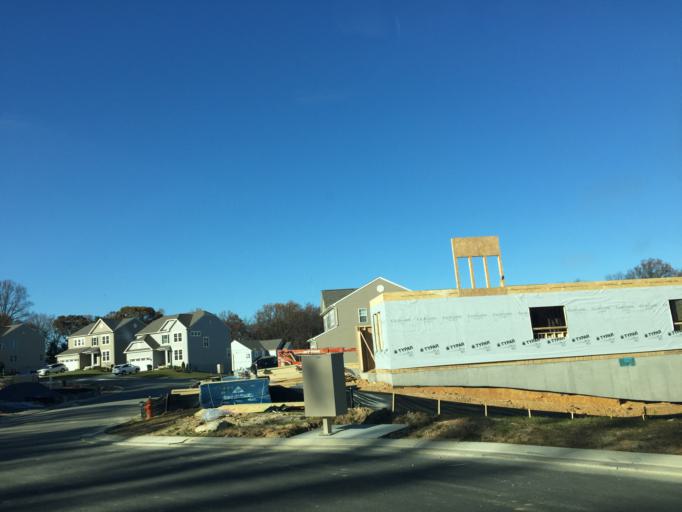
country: US
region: Maryland
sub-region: Baltimore County
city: Parkville
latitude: 39.4037
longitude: -76.5514
